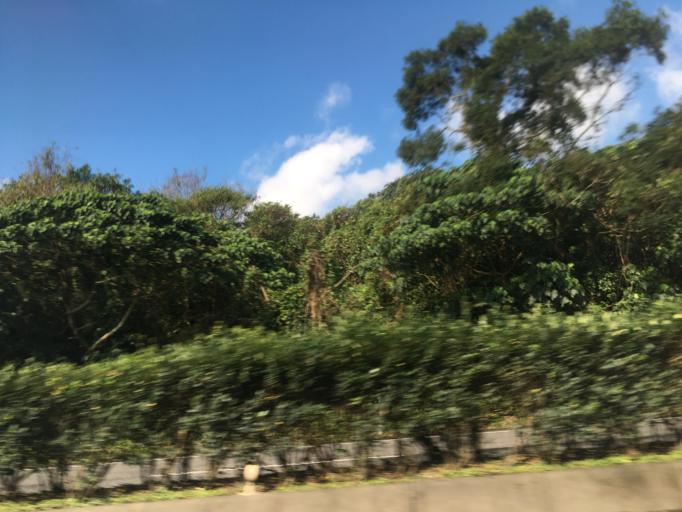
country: TW
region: Taiwan
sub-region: Yilan
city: Yilan
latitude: 24.9326
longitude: 121.8844
